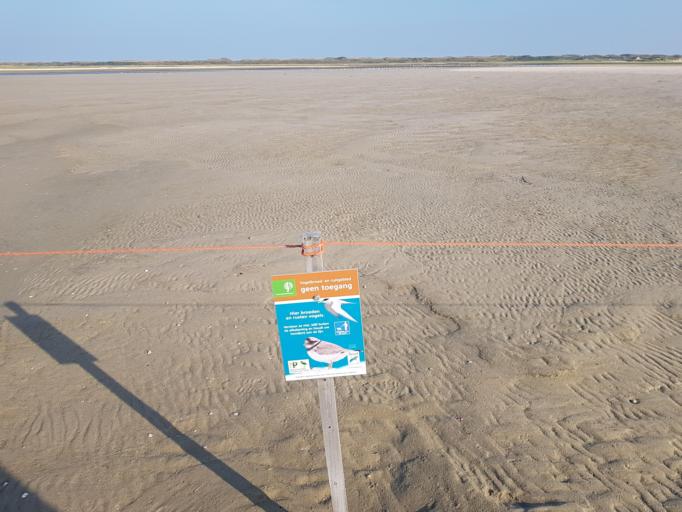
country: NL
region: North Holland
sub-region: Gemeente Texel
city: Den Burg
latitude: 53.1385
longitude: 4.7998
